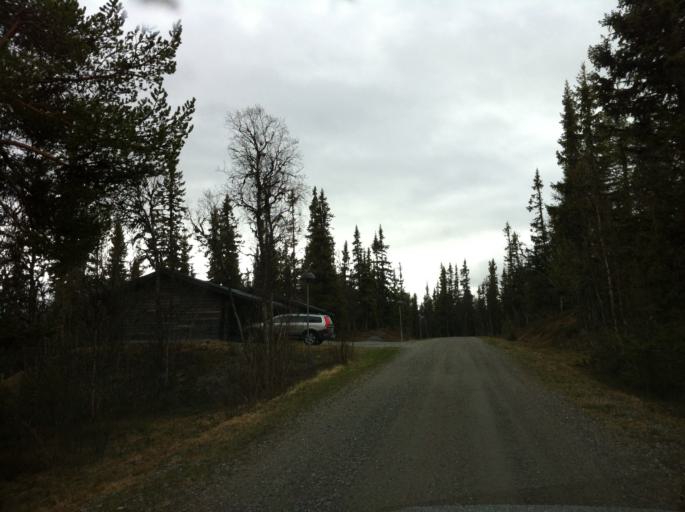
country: NO
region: Hedmark
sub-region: Engerdal
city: Engerdal
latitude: 62.5424
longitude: 12.4446
